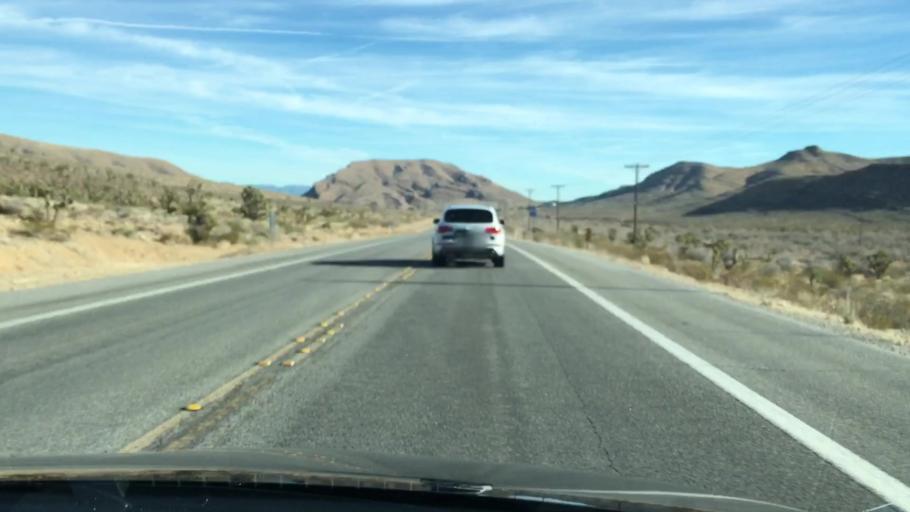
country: US
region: Nevada
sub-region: Clark County
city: Summerlin South
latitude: 36.0621
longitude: -115.4306
